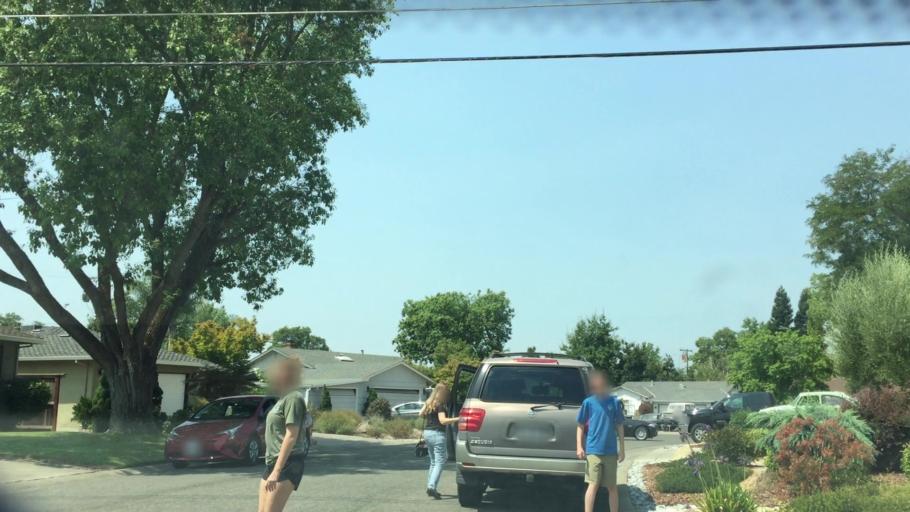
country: US
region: California
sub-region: Sacramento County
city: Arden-Arcade
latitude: 38.6011
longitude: -121.3584
